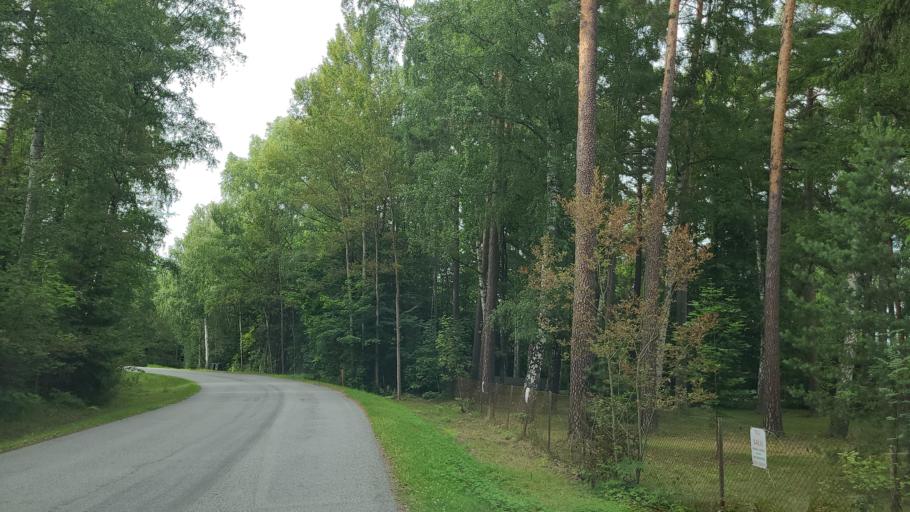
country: SE
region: Stockholm
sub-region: Upplands-Bro Kommun
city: Bro
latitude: 59.4876
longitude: 17.5689
